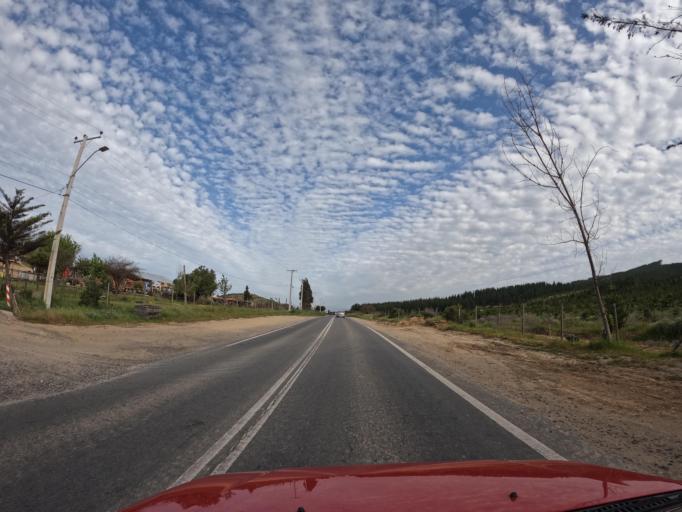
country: CL
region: O'Higgins
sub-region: Provincia de Colchagua
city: Santa Cruz
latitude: -34.3190
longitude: -71.7622
